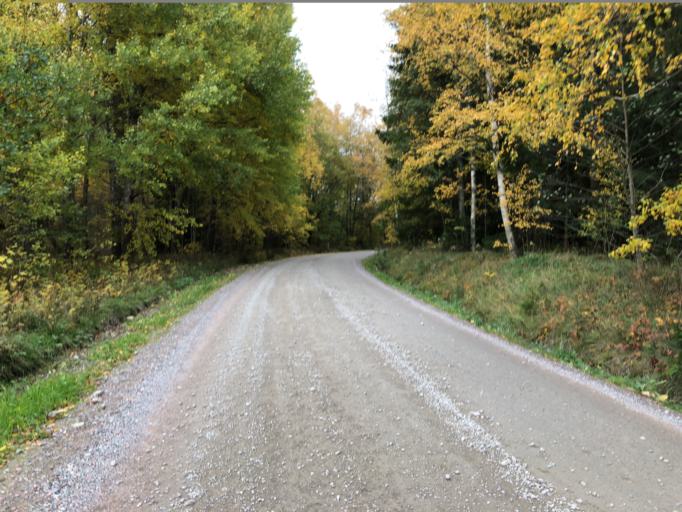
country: SE
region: Soedermanland
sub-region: Oxelosunds Kommun
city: Bara
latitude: 58.7165
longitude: 17.0406
